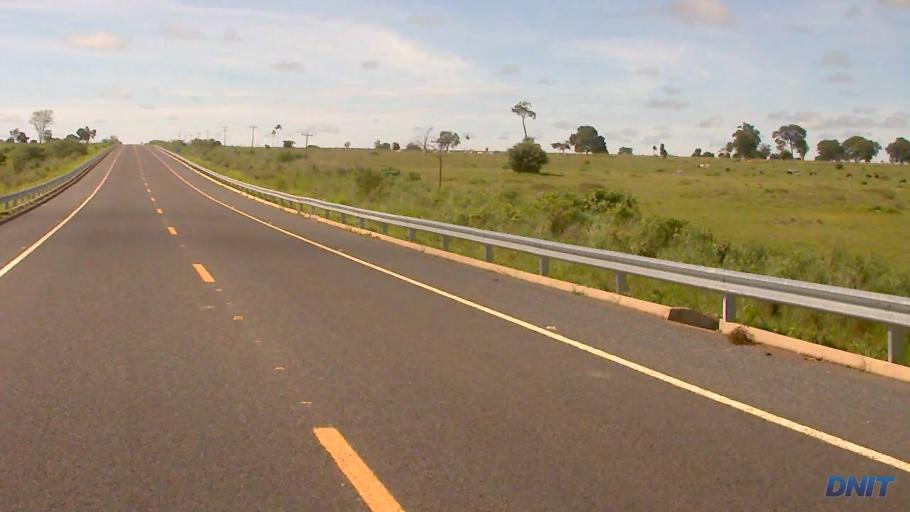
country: BR
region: Goias
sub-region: Sao Miguel Do Araguaia
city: Sao Miguel do Araguaia
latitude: -13.3444
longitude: -50.1512
